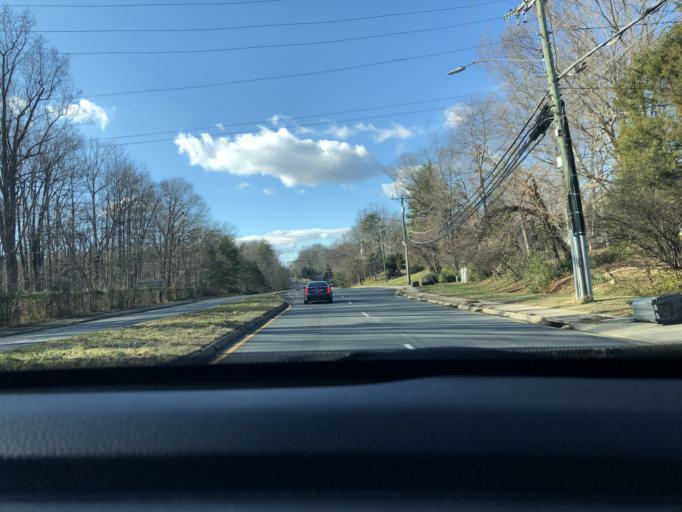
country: US
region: Virginia
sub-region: City of Fairfax
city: Fairfax
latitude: 38.8265
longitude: -77.2905
